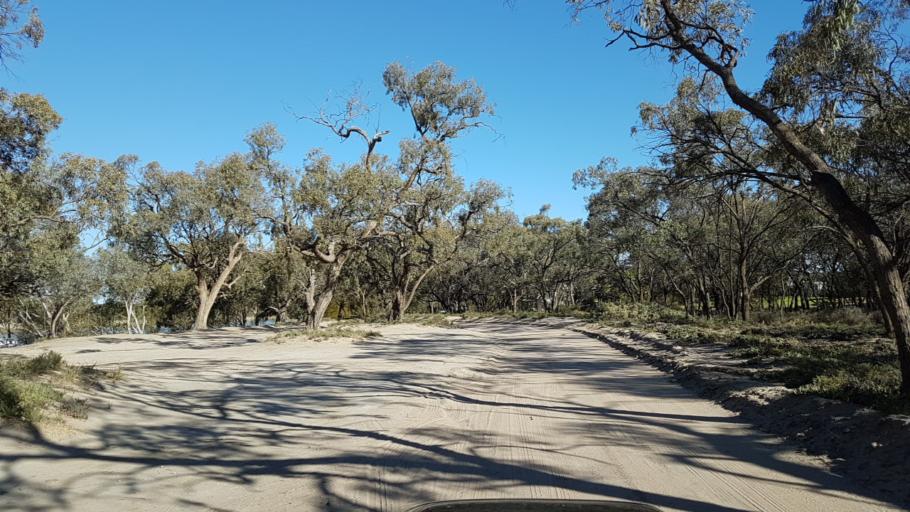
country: AU
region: South Australia
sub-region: Loxton Waikerie
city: Waikerie
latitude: -34.1620
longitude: 140.0323
